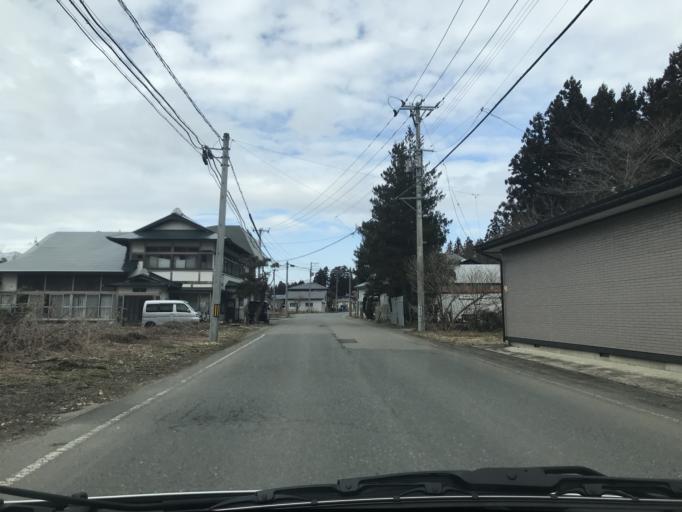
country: JP
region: Iwate
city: Kitakami
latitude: 39.3143
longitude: 140.9871
